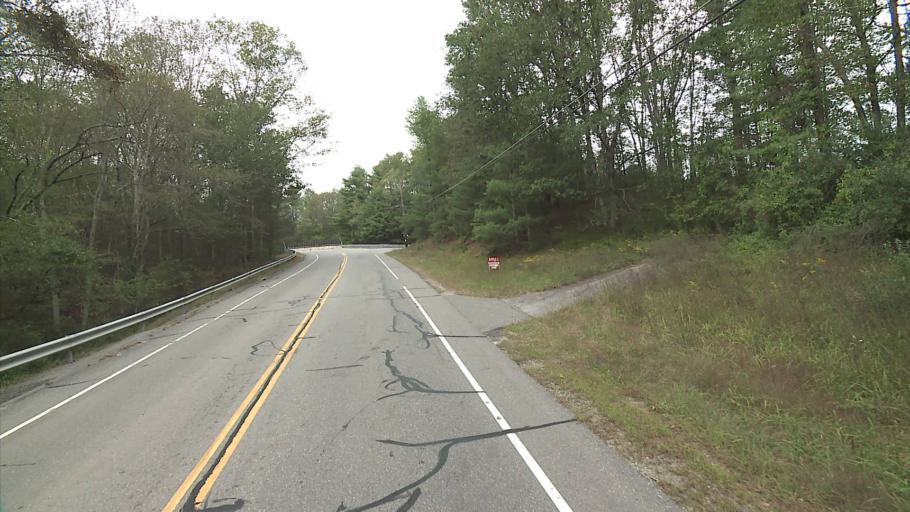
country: US
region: Connecticut
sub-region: New London County
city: Jewett City
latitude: 41.6496
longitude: -71.9635
